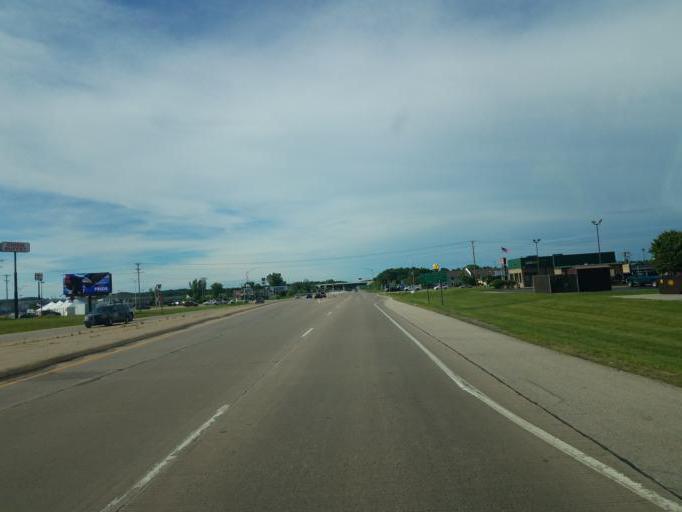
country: US
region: Wisconsin
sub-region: Monroe County
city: Tomah
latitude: 44.0162
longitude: -90.5050
